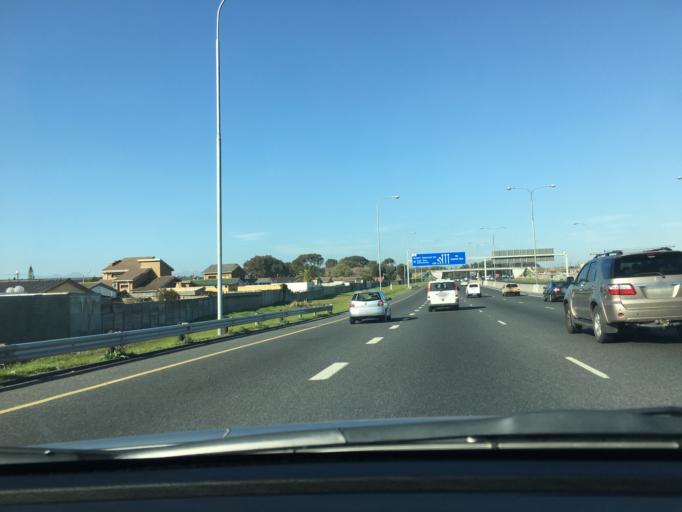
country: ZA
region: Western Cape
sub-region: City of Cape Town
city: Lansdowne
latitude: -33.9622
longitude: 18.5643
